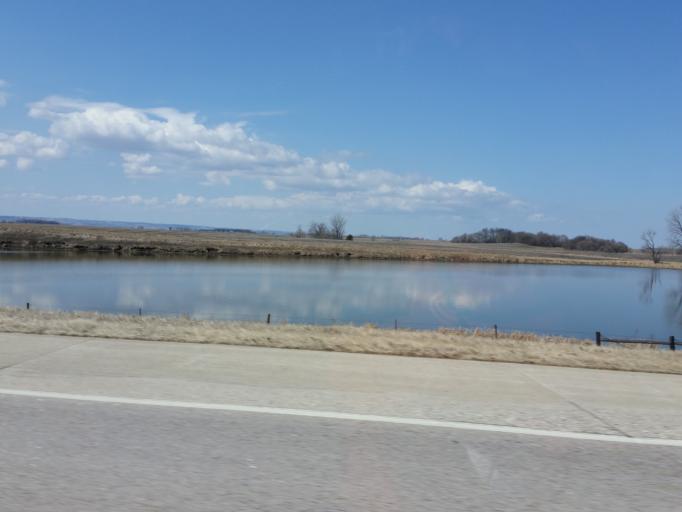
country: US
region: South Dakota
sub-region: Roberts County
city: Sisseton
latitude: 45.7269
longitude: -96.9450
